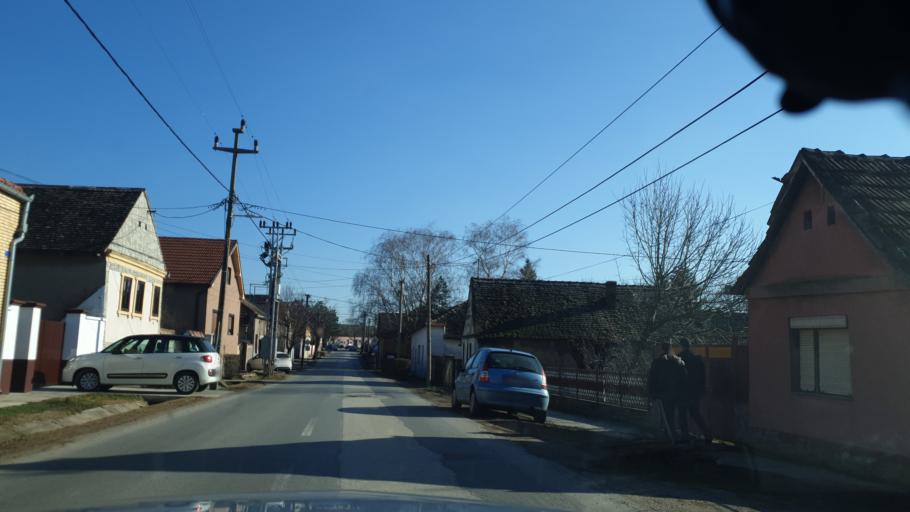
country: RS
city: Vrdnik
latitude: 45.1236
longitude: 19.7925
